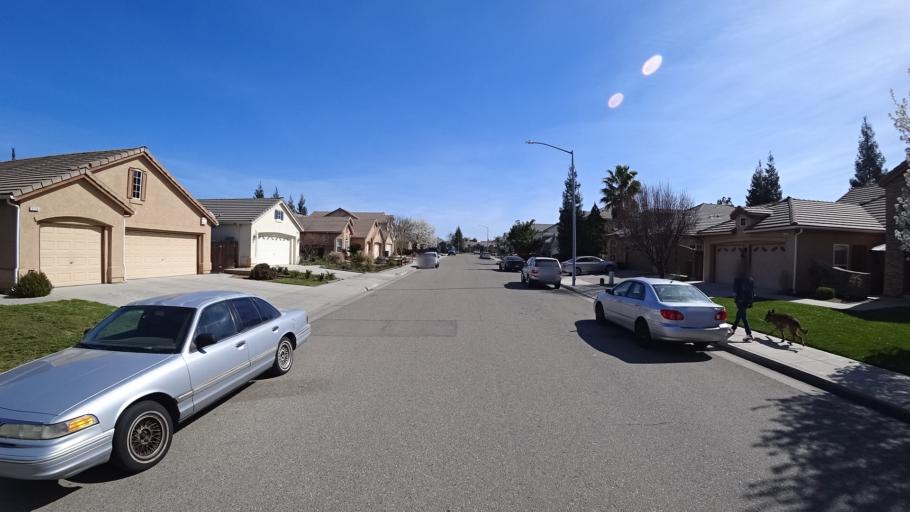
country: US
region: California
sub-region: Fresno County
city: Clovis
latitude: 36.8904
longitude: -119.7632
